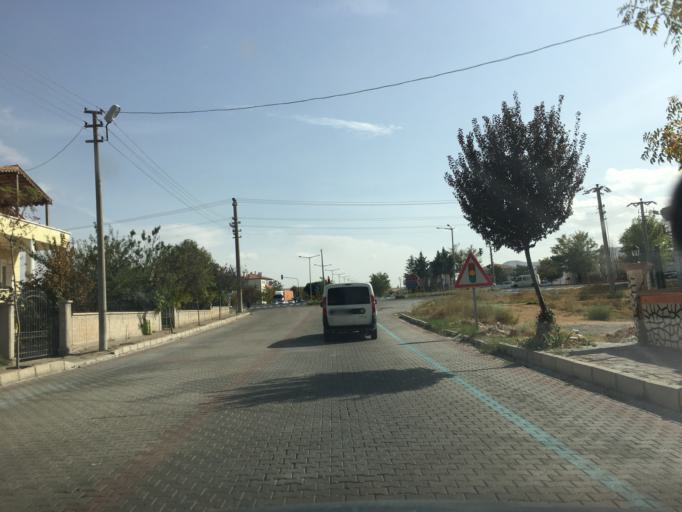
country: TR
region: Nevsehir
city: Avanos
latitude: 38.7057
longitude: 34.8542
